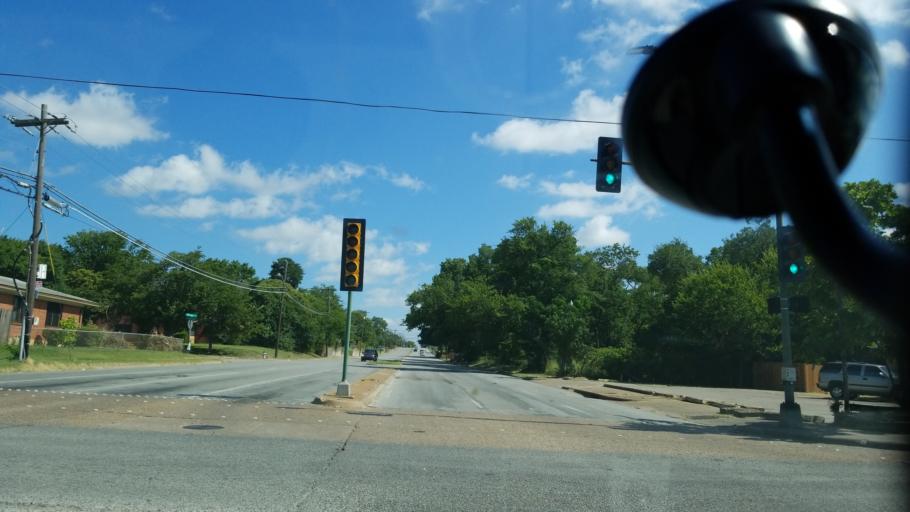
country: US
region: Texas
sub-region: Dallas County
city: Cockrell Hill
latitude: 32.6913
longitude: -96.8147
